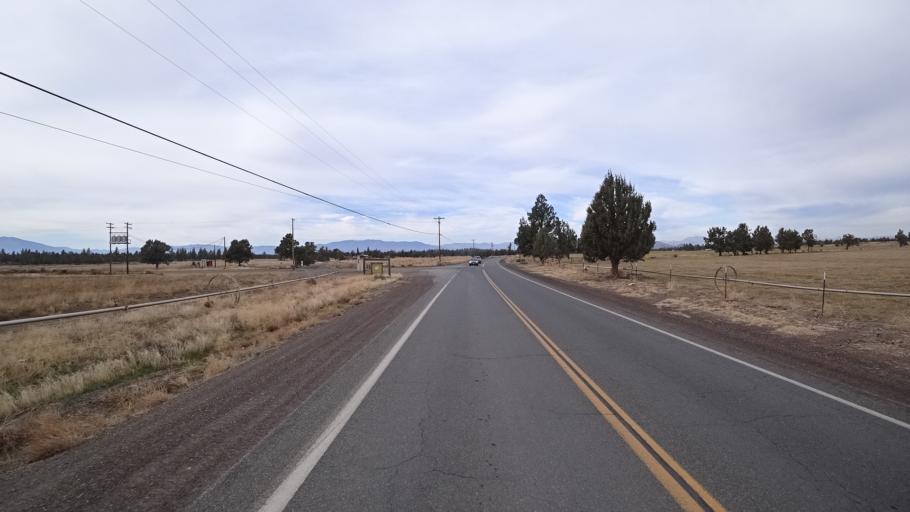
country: US
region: California
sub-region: Siskiyou County
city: Weed
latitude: 41.5968
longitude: -122.3396
